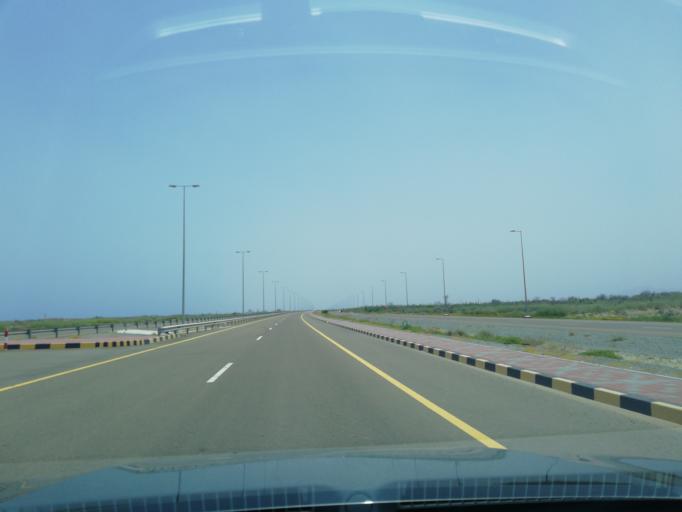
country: OM
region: Al Batinah
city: Shinas
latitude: 24.8907
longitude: 56.4009
